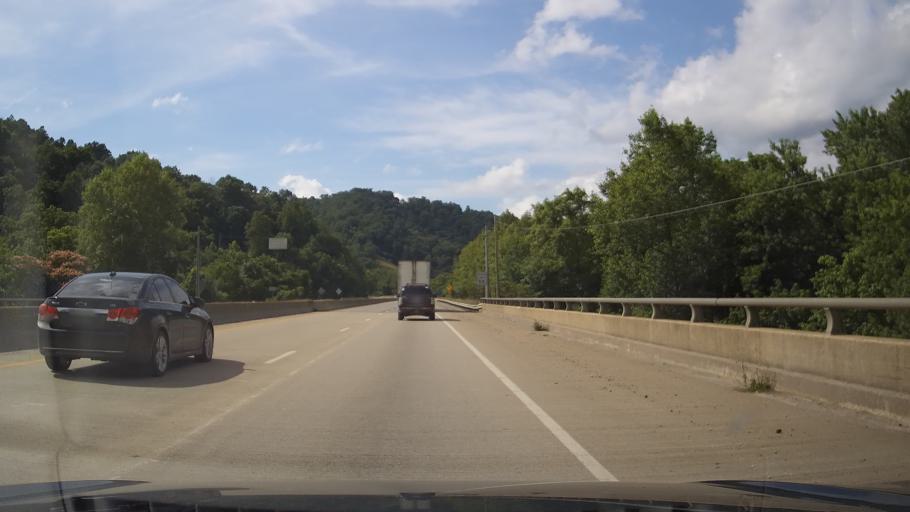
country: US
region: Kentucky
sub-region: Floyd County
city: Prestonsburg
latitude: 37.6189
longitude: -82.7231
